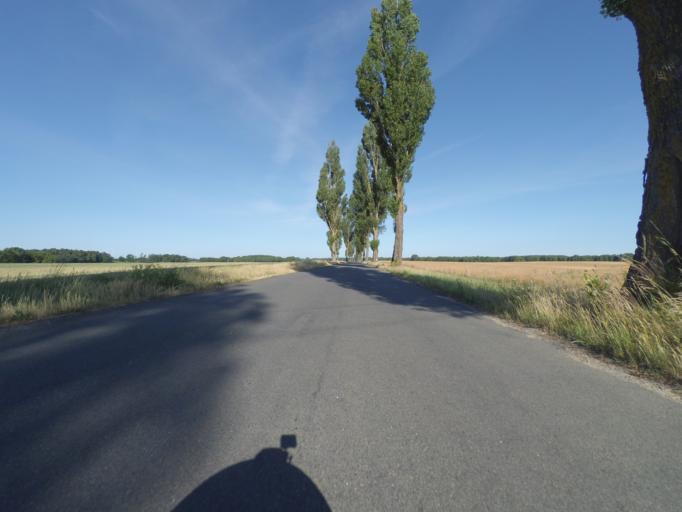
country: DE
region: Mecklenburg-Vorpommern
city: Lubz
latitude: 53.3688
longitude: 12.0932
